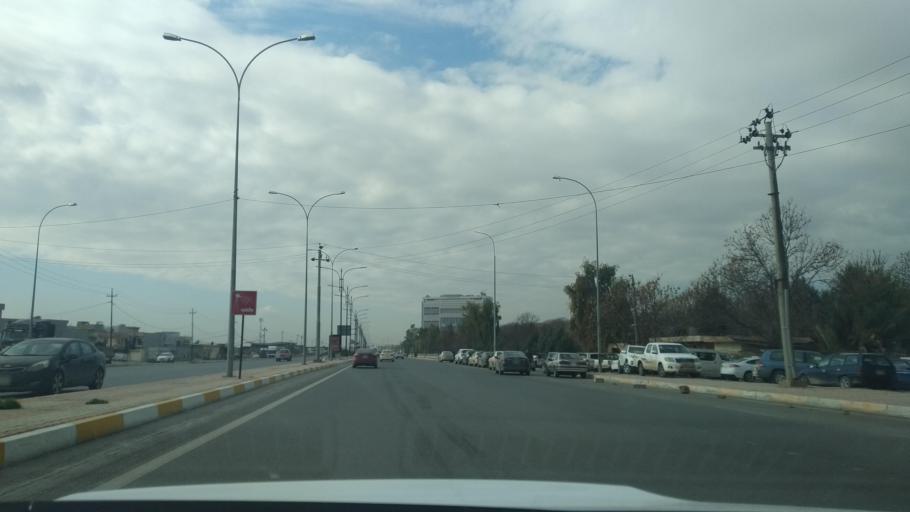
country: IQ
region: Arbil
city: Erbil
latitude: 36.1898
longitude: 43.9924
